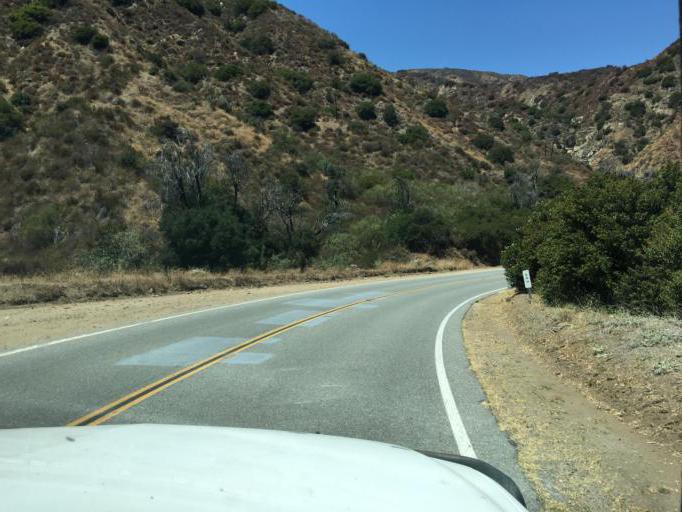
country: US
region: California
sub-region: Los Angeles County
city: Glendora
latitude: 34.1913
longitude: -117.8659
